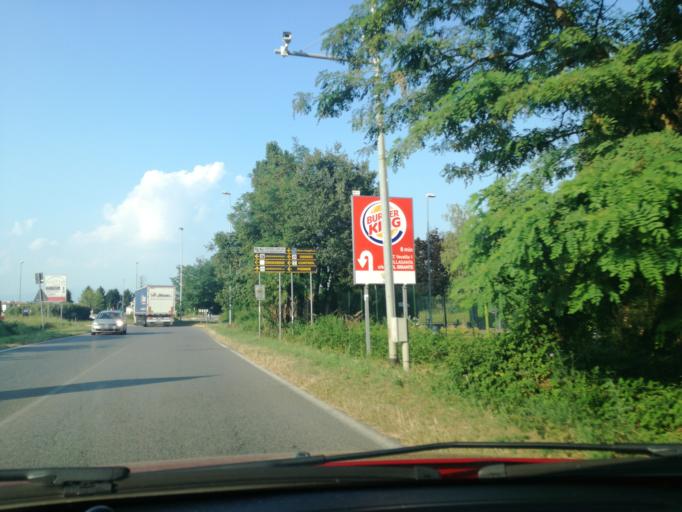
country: IT
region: Lombardy
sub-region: Provincia di Monza e Brianza
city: Velasca
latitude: 45.6415
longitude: 9.3456
